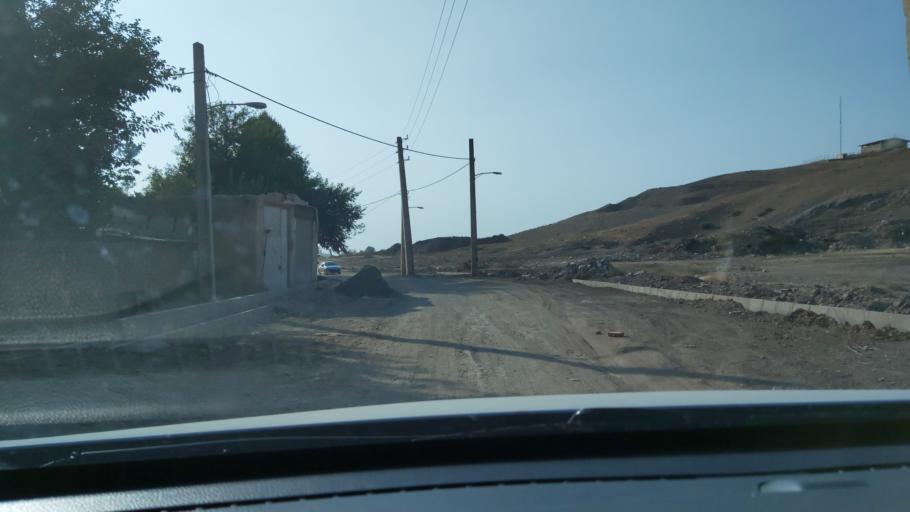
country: IR
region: Alborz
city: Hashtgerd
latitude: 35.9539
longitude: 50.7875
